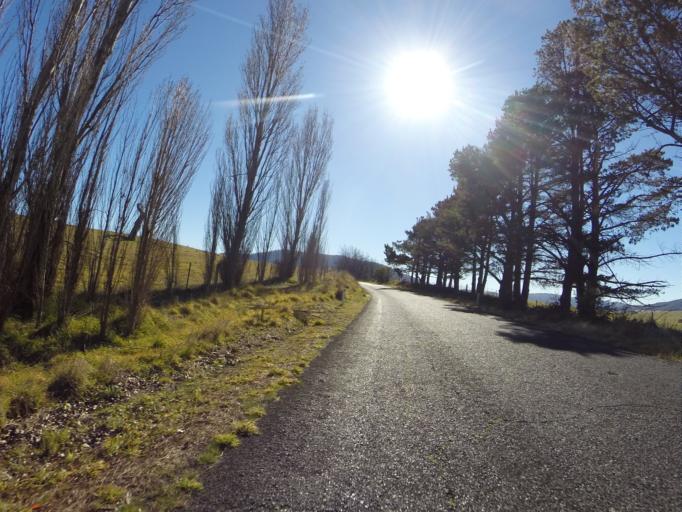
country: AU
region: New South Wales
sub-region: Oberon
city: Oberon
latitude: -33.5542
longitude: 149.8717
